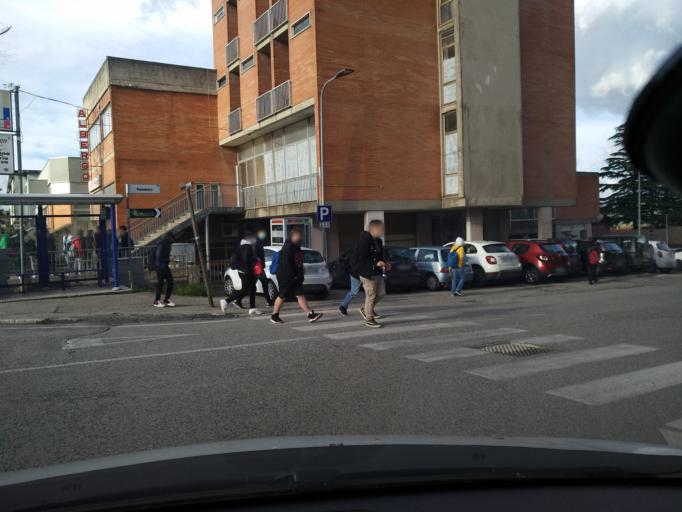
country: IT
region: The Marches
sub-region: Provincia di Pesaro e Urbino
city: Urbino
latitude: 43.7342
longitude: 12.6319
